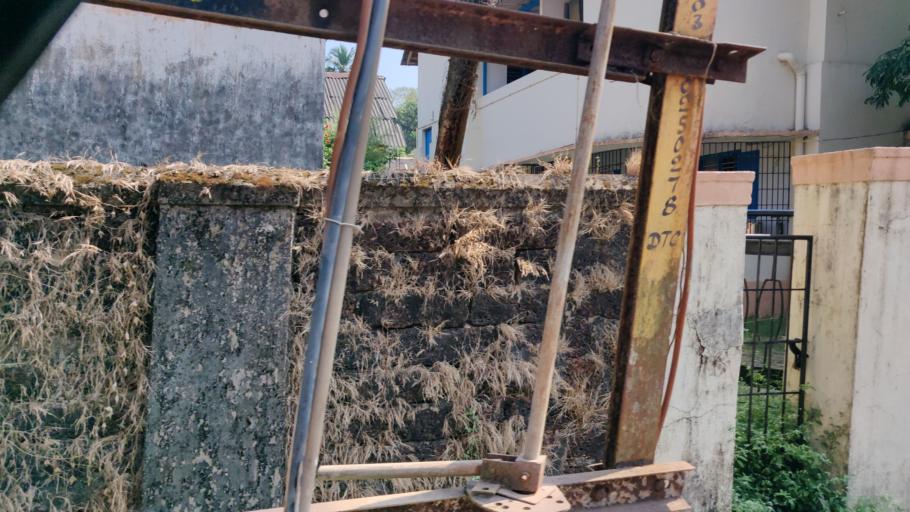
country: IN
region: Karnataka
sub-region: Dakshina Kannada
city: Ullal
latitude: 12.8592
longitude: 74.8340
